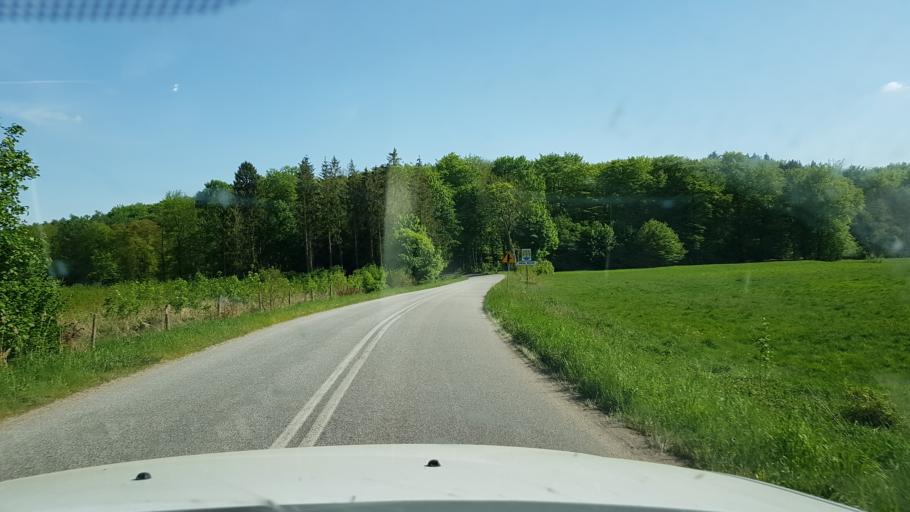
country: PL
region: West Pomeranian Voivodeship
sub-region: Powiat lobeski
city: Resko
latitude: 53.8419
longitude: 15.3728
